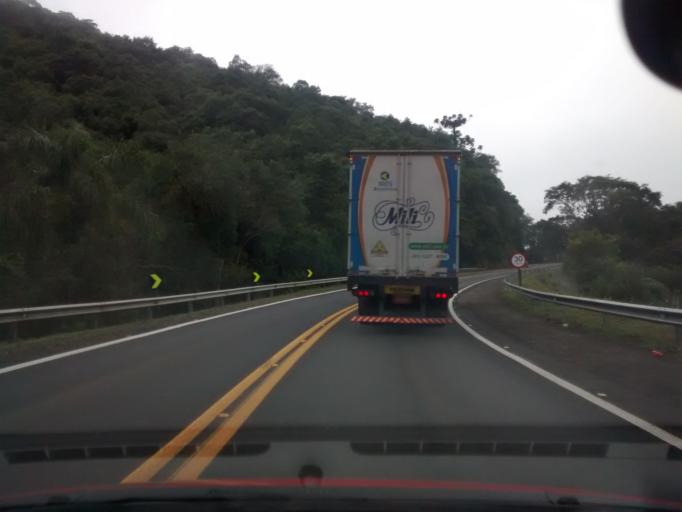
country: BR
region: Rio Grande do Sul
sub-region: Vacaria
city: Estrela
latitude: -28.1979
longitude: -50.7290
